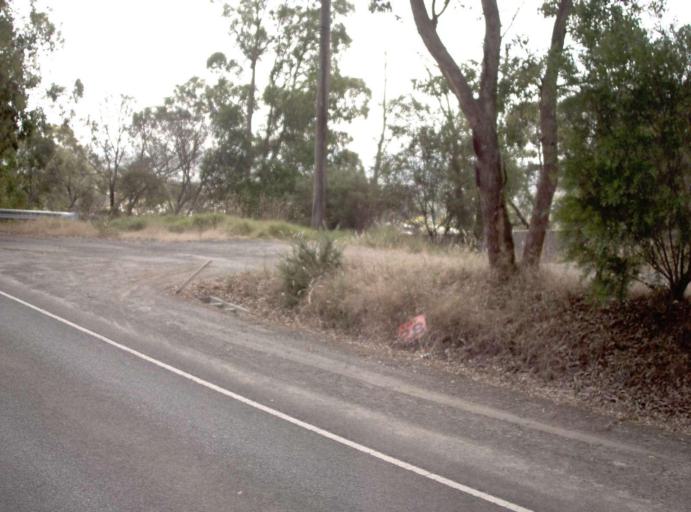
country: AU
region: Victoria
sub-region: Yarra Ranges
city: Lysterfield
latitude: -37.9262
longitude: 145.2805
